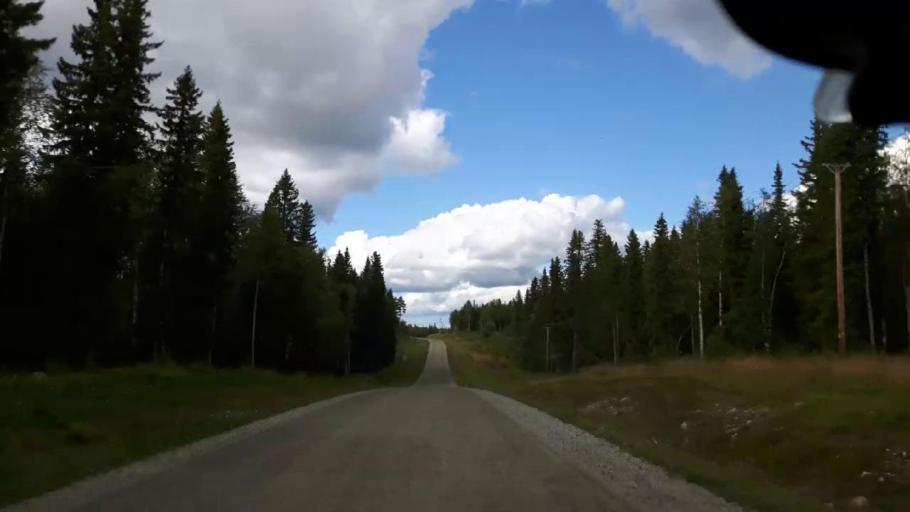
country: SE
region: Jaemtland
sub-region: Stroemsunds Kommun
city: Stroemsund
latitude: 63.3705
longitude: 15.5652
